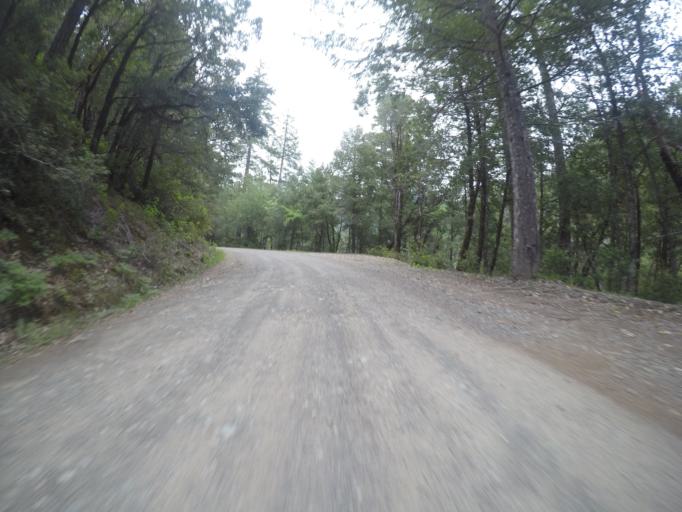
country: US
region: California
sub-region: Del Norte County
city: Bertsch-Oceanview
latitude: 41.7378
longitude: -123.8792
